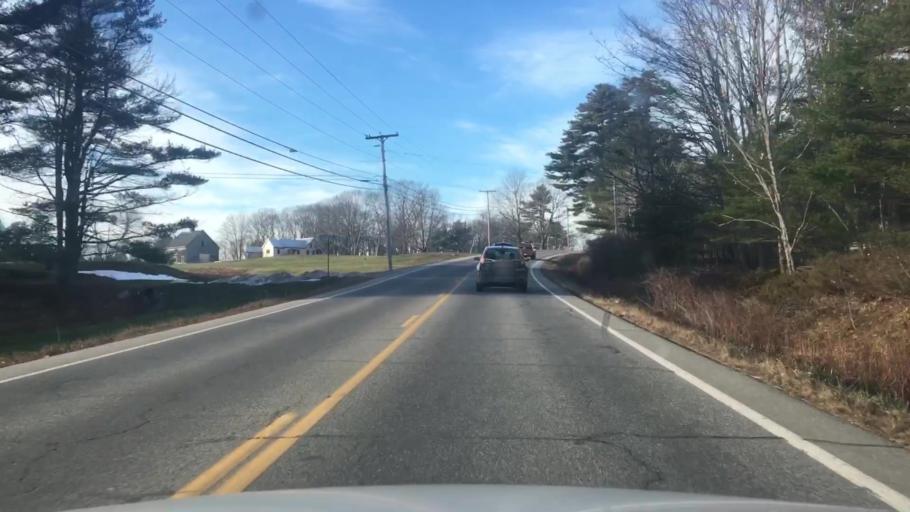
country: US
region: Maine
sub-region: Lincoln County
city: Edgecomb
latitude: 43.9328
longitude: -69.6198
